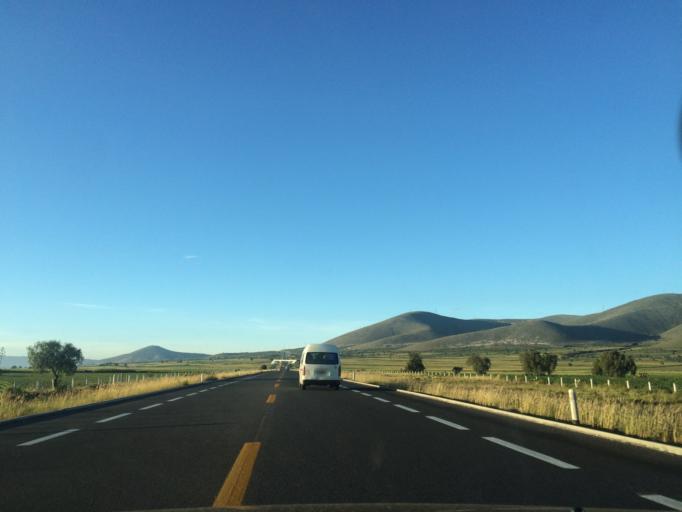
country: MX
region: Puebla
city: Morelos Canada
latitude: 18.7527
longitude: -97.4805
